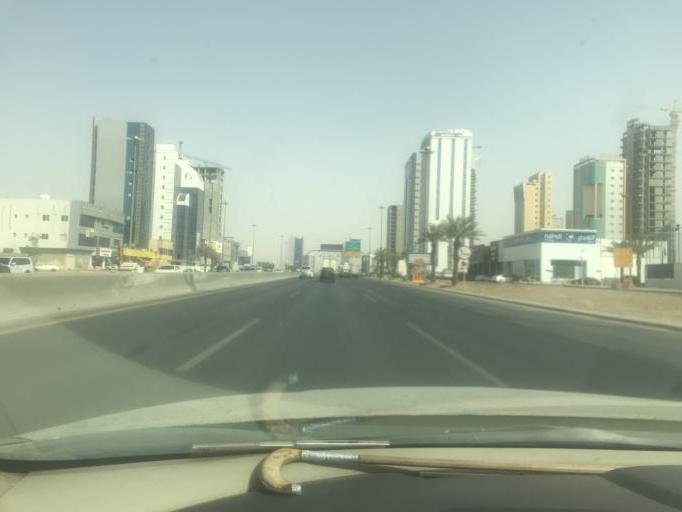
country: SA
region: Ar Riyad
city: Riyadh
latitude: 24.8031
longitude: 46.6261
